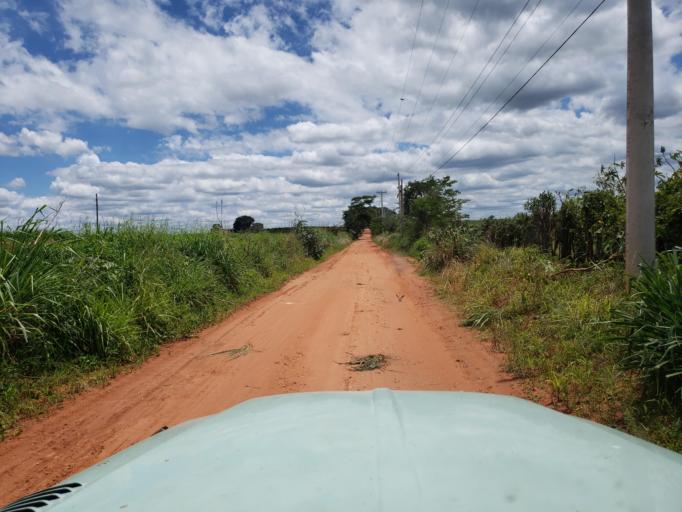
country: BR
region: Sao Paulo
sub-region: Aguai
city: Aguai
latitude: -22.1992
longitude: -46.9573
